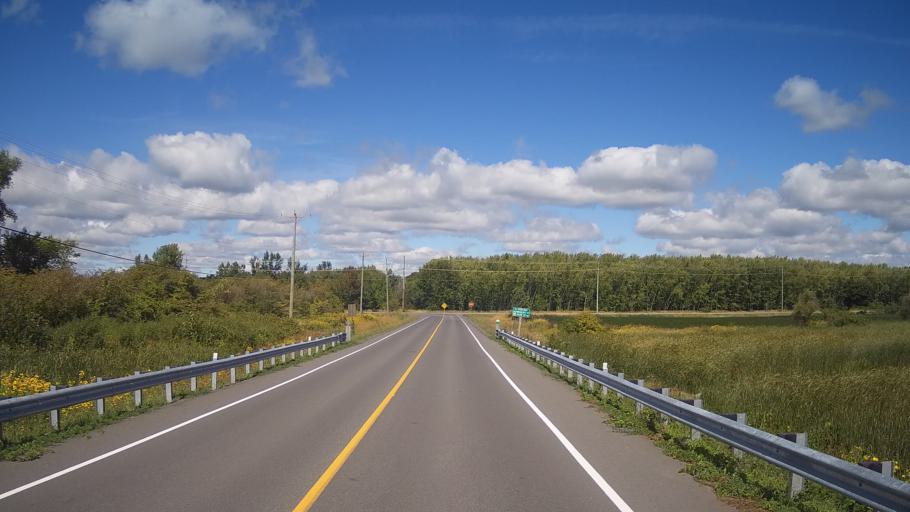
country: US
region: New York
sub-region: St. Lawrence County
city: Ogdensburg
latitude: 44.8617
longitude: -75.2758
